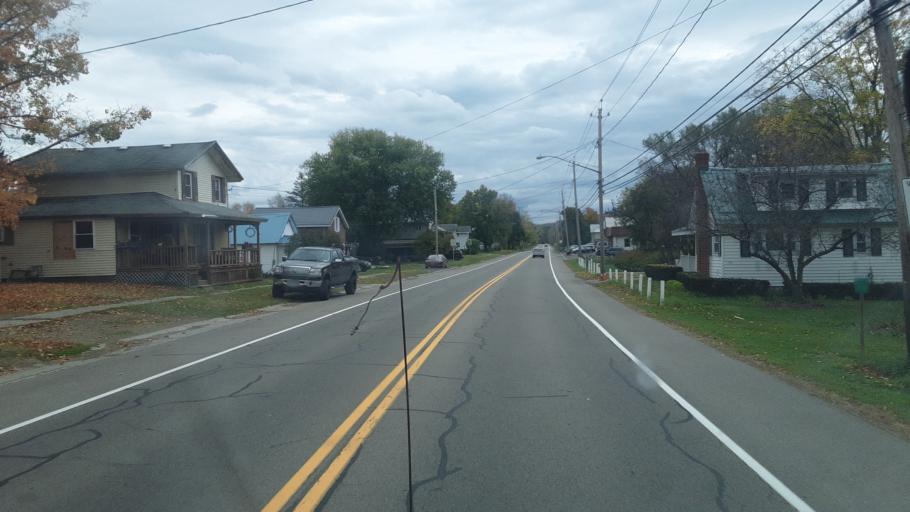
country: US
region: New York
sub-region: Allegany County
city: Belmont
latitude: 42.2210
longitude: -78.0241
